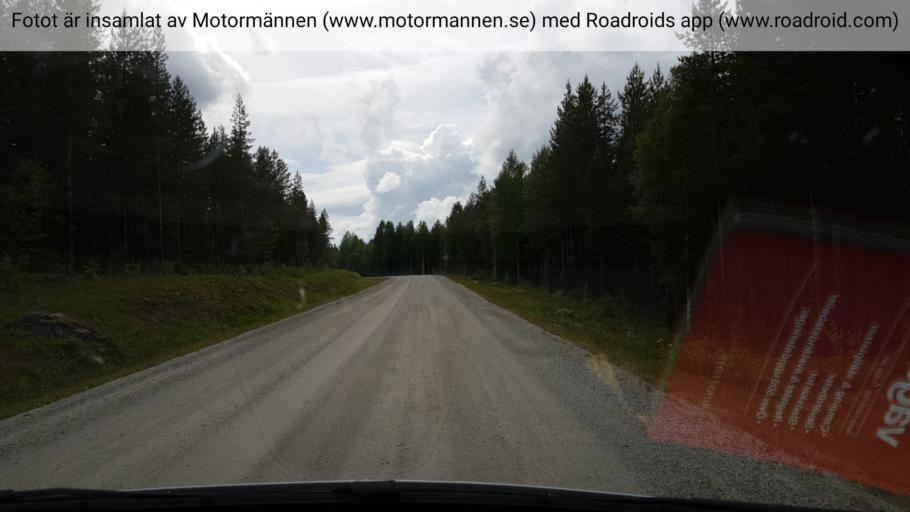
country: SE
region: Vaesternorrland
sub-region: Solleftea Kommun
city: Solleftea
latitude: 63.3795
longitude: 17.4873
